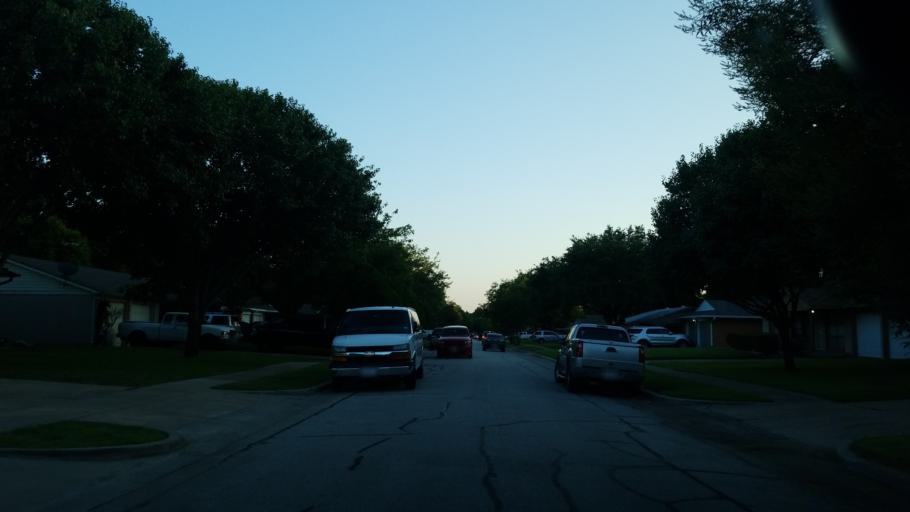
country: US
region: Texas
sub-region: Dallas County
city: Farmers Branch
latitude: 32.9328
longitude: -96.8824
